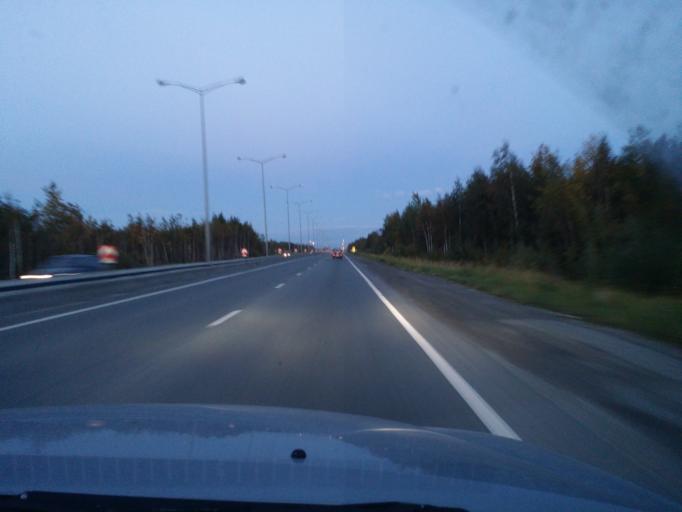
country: RU
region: Khanty-Mansiyskiy Avtonomnyy Okrug
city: Nizhnevartovsk
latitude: 60.9828
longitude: 76.4873
